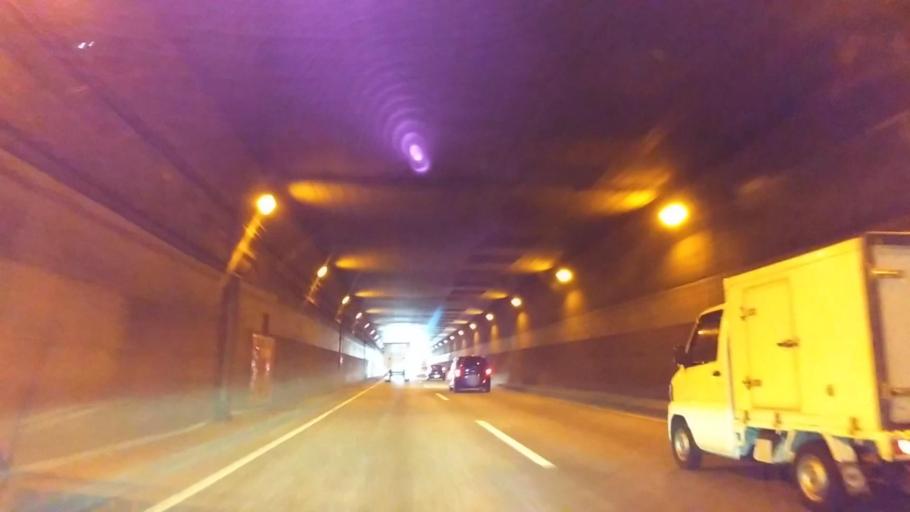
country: JP
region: Kanagawa
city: Minami-rinkan
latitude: 35.4877
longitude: 139.4617
